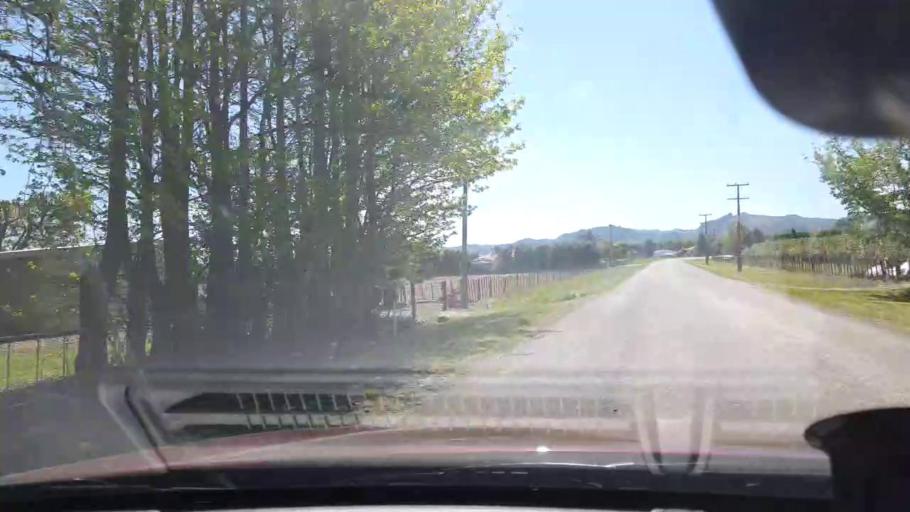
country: NZ
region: Gisborne
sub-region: Gisborne District
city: Gisborne
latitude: -38.6381
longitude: 177.9397
